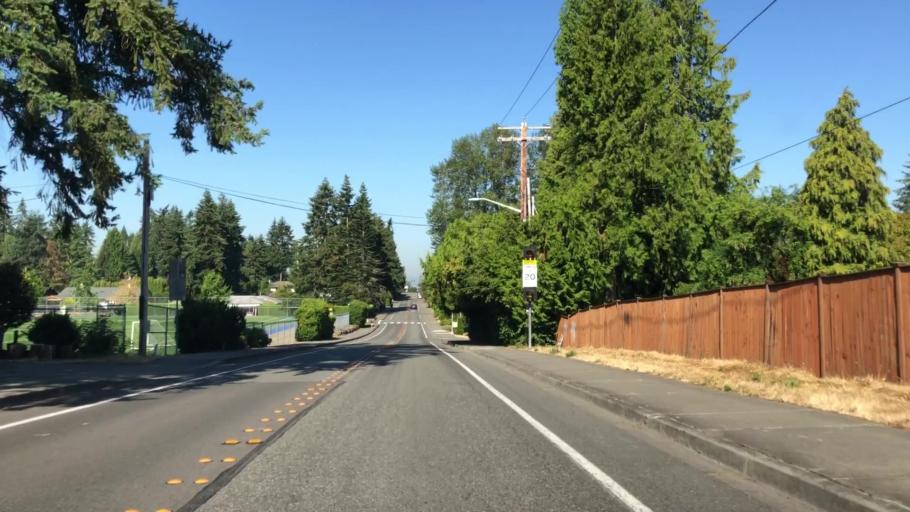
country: US
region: Washington
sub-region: King County
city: Eastgate
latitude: 47.6026
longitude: -122.1477
